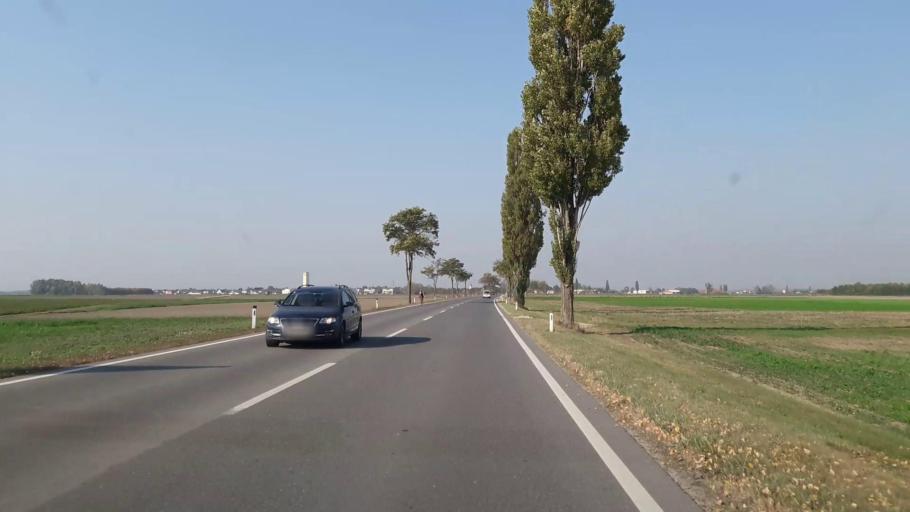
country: AT
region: Lower Austria
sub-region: Politischer Bezirk Ganserndorf
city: Engelhartstetten
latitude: 48.1646
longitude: 16.8957
